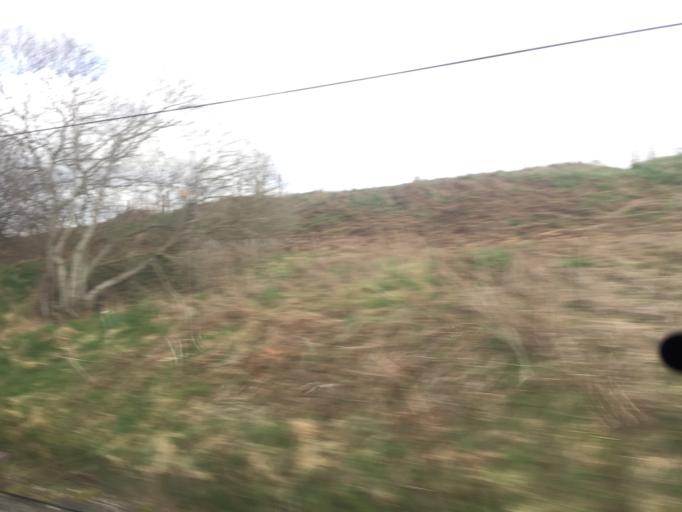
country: GB
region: England
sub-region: Cumbria
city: Scotby
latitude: 54.8430
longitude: -2.8834
